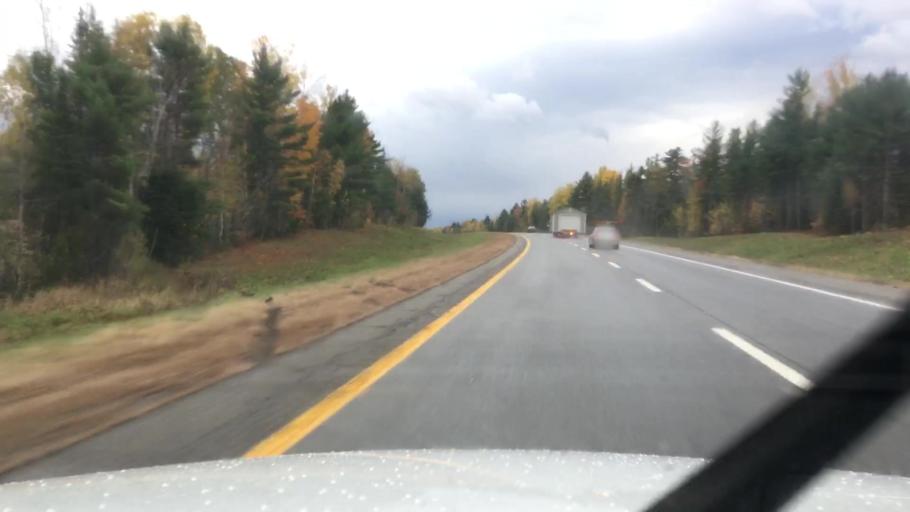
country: US
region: Maine
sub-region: Penobscot County
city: Howland
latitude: 45.2625
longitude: -68.6808
